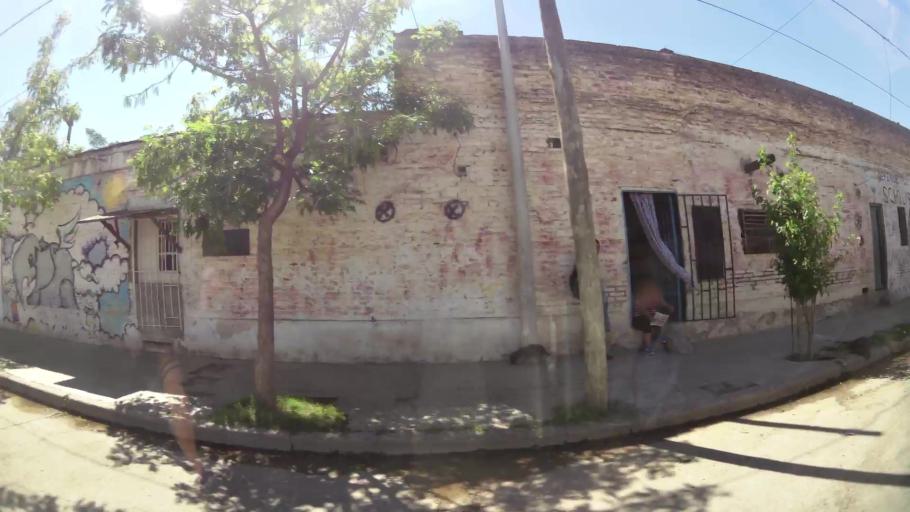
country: AR
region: Cordoba
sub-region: Departamento de Capital
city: Cordoba
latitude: -31.4185
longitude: -64.1372
